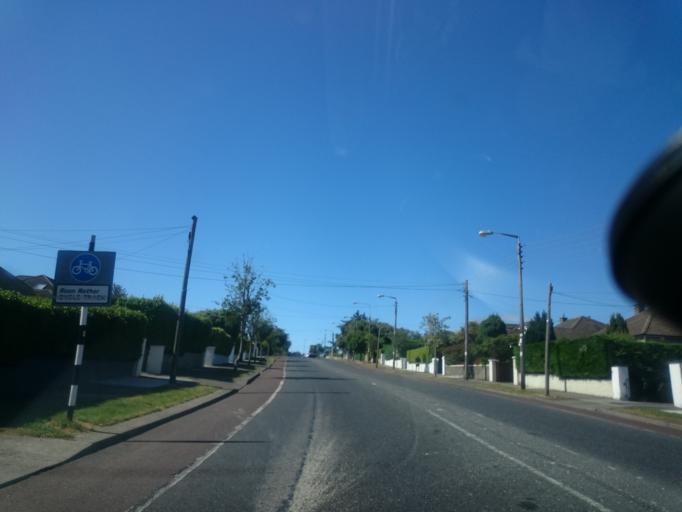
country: IE
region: Leinster
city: Sallynoggin
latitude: 53.2754
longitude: -6.1224
